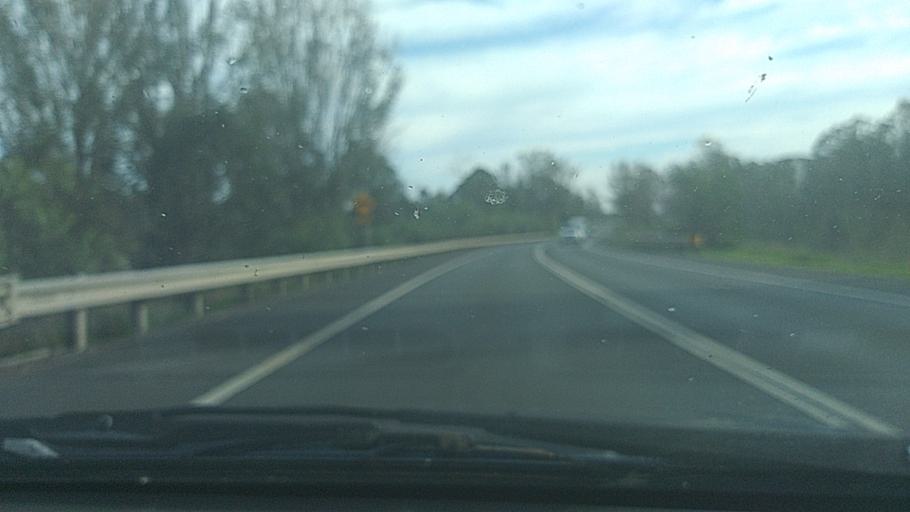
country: AU
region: New South Wales
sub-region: Penrith Municipality
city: Mulgoa
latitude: -33.8277
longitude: 150.6833
